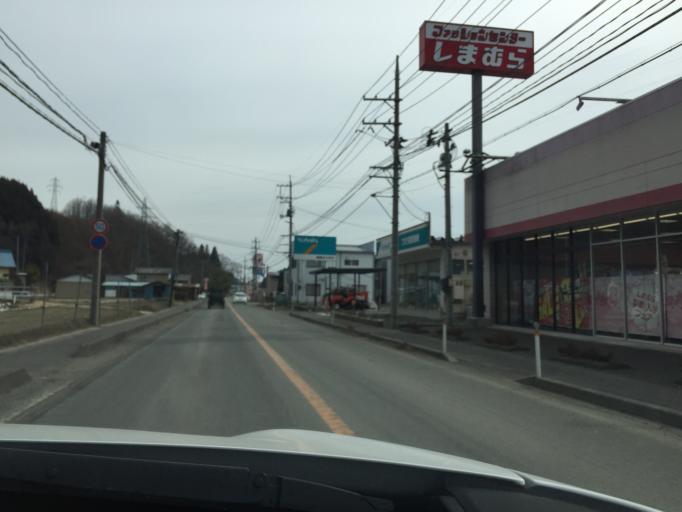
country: JP
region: Fukushima
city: Funehikimachi-funehiki
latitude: 37.2969
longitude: 140.6203
